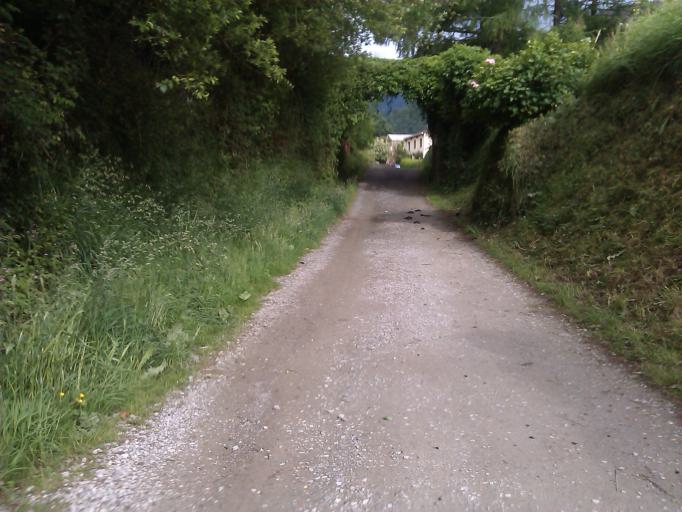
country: ES
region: Navarre
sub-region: Provincia de Navarra
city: Leitza
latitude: 43.0857
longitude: -1.9140
